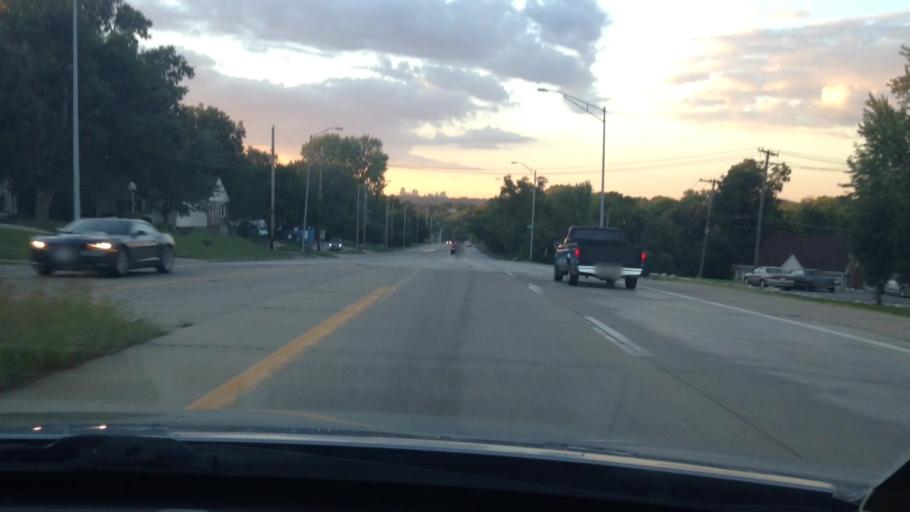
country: US
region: Missouri
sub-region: Jackson County
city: Raytown
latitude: 39.0240
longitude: -94.5036
